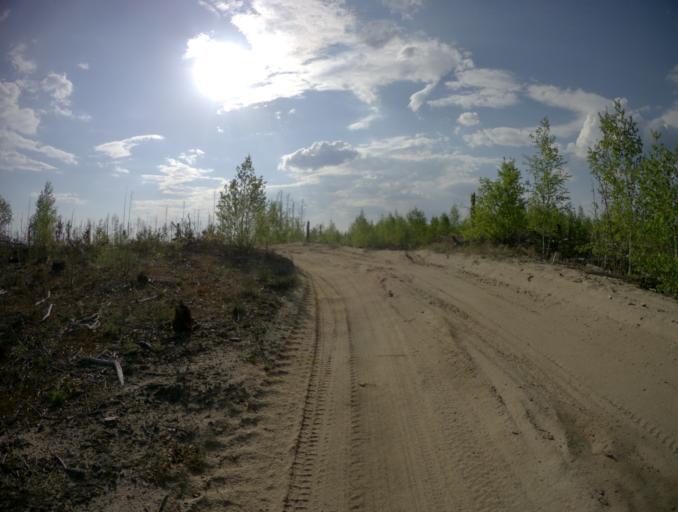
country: RU
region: Ivanovo
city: Talitsy
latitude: 56.4151
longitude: 42.2571
